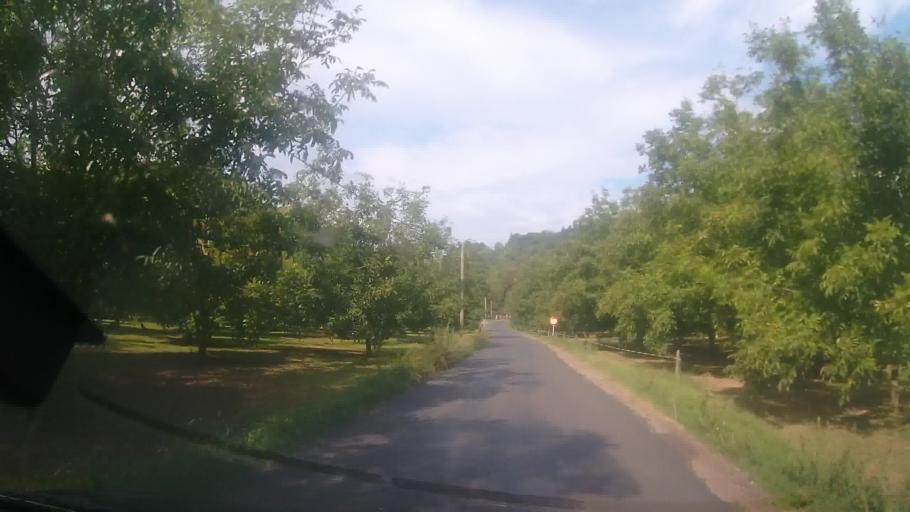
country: FR
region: Aquitaine
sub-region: Departement de la Dordogne
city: Cenac-et-Saint-Julien
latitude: 44.7953
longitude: 1.1644
